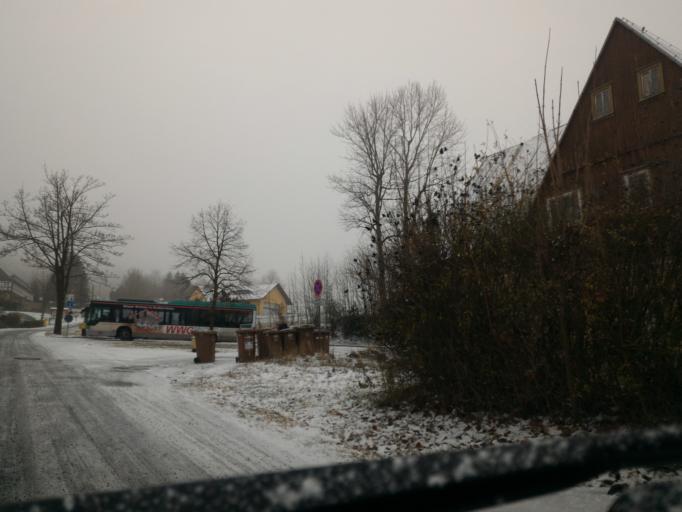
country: DE
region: Saxony
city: Grossschonau
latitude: 50.8546
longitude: 14.6548
